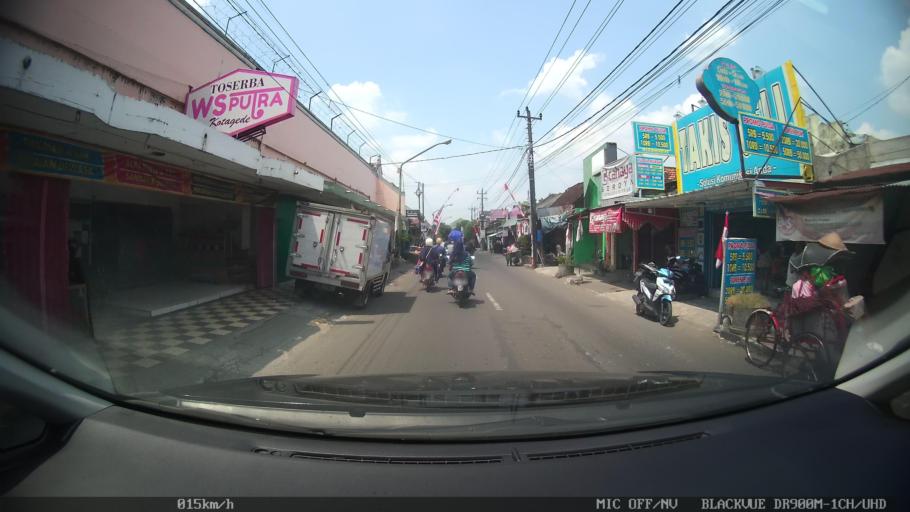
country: ID
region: Daerah Istimewa Yogyakarta
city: Yogyakarta
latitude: -7.8273
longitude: 110.4020
